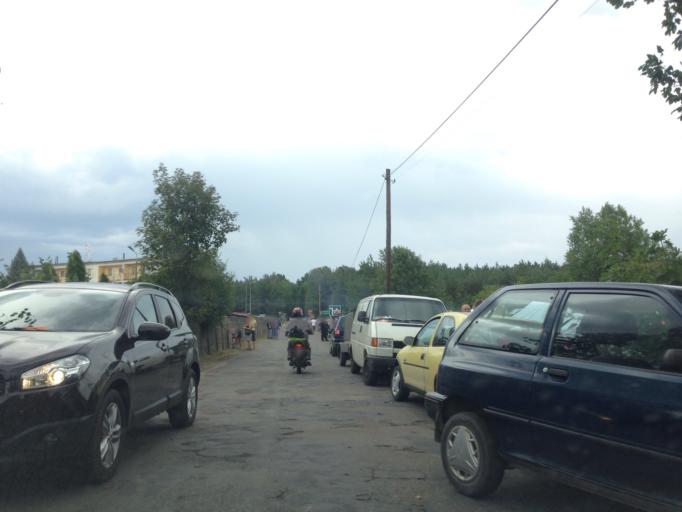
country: PL
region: Kujawsko-Pomorskie
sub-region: Powiat swiecki
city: Lniano
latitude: 53.5431
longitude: 18.1194
